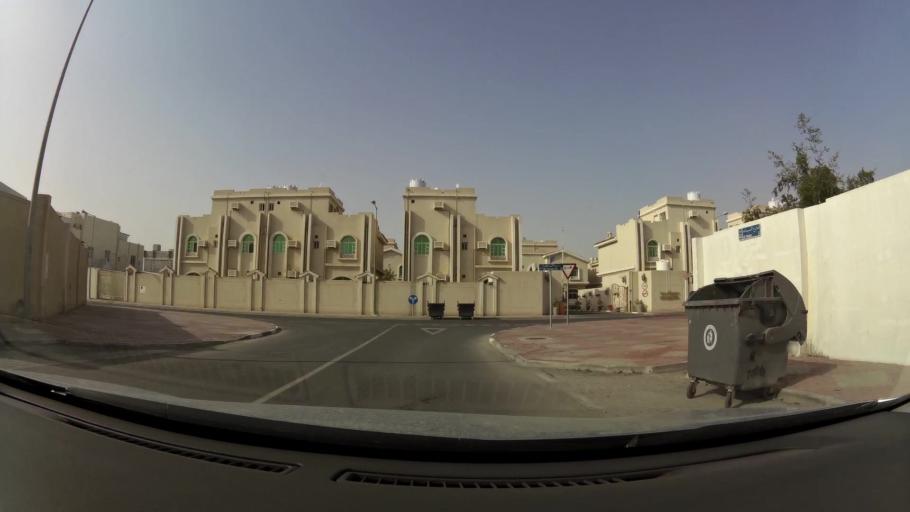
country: QA
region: Baladiyat ar Rayyan
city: Ar Rayyan
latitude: 25.2400
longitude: 51.4381
